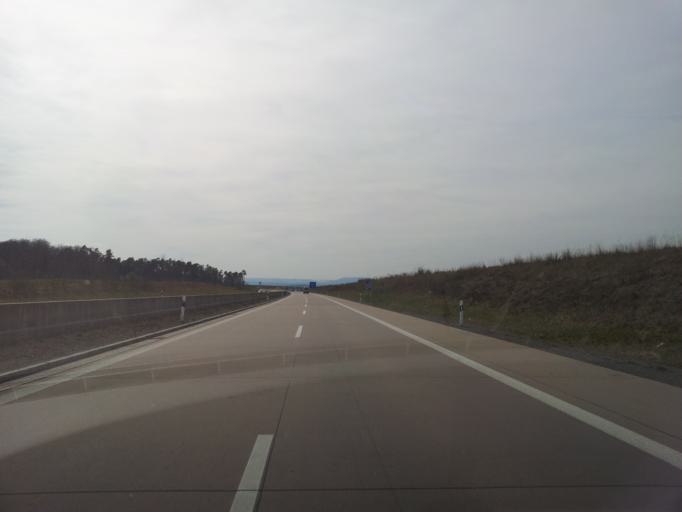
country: DE
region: Bavaria
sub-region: Regierungsbezirk Unterfranken
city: Hendungen
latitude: 50.4261
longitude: 10.3634
